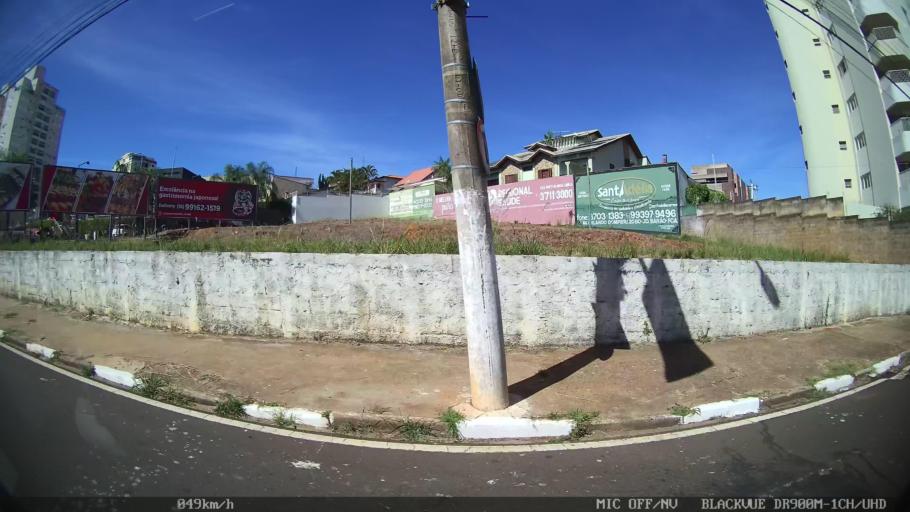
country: BR
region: Sao Paulo
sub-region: Franca
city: Franca
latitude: -20.5386
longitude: -47.3917
